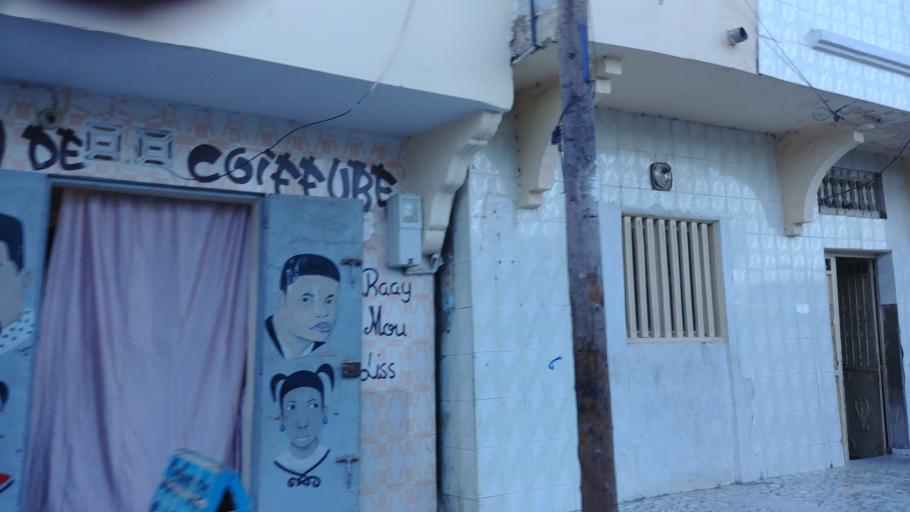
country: SN
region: Saint-Louis
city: Saint-Louis
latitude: 16.0016
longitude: -16.4875
